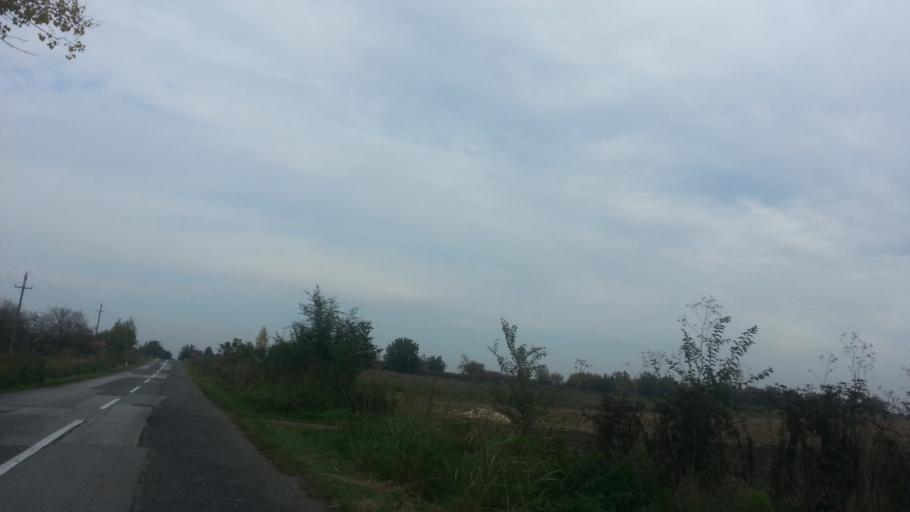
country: RS
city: Surduk
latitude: 45.0594
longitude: 20.3308
